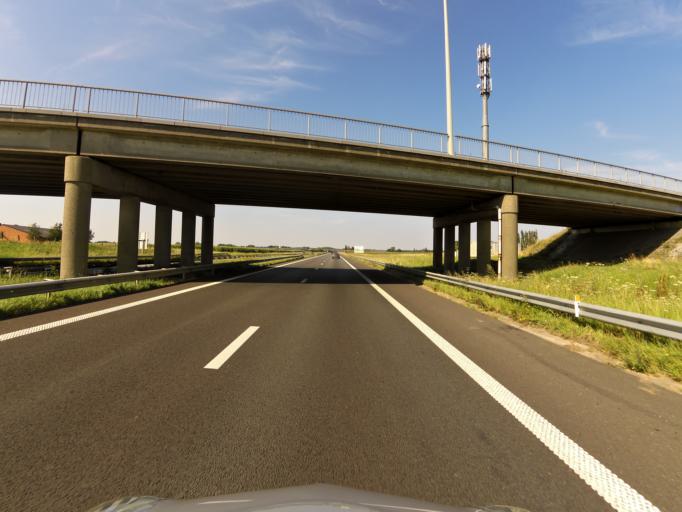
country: BE
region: Flanders
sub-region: Provincie West-Vlaanderen
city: Lichtervelde
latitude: 51.0354
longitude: 3.1644
